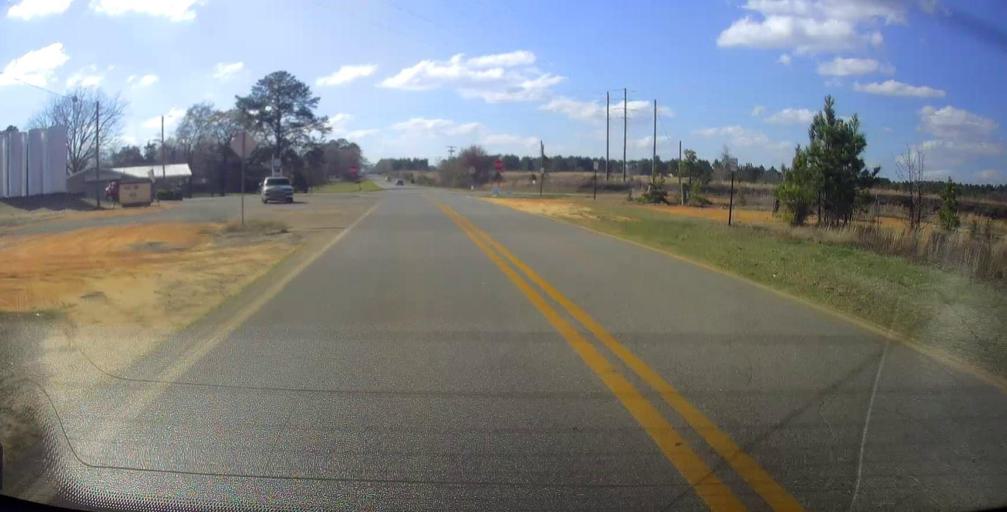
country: US
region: Georgia
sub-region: Laurens County
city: Dublin
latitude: 32.5683
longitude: -83.0324
